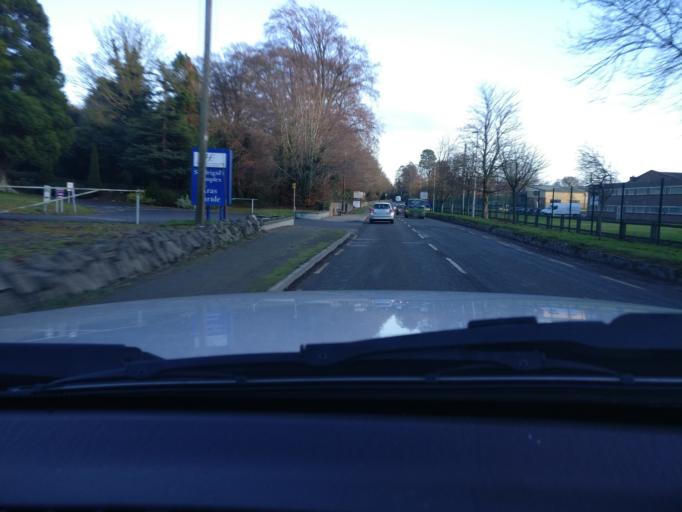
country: IE
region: Leinster
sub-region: Lu
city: Ardee
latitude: 53.8559
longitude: -6.5499
